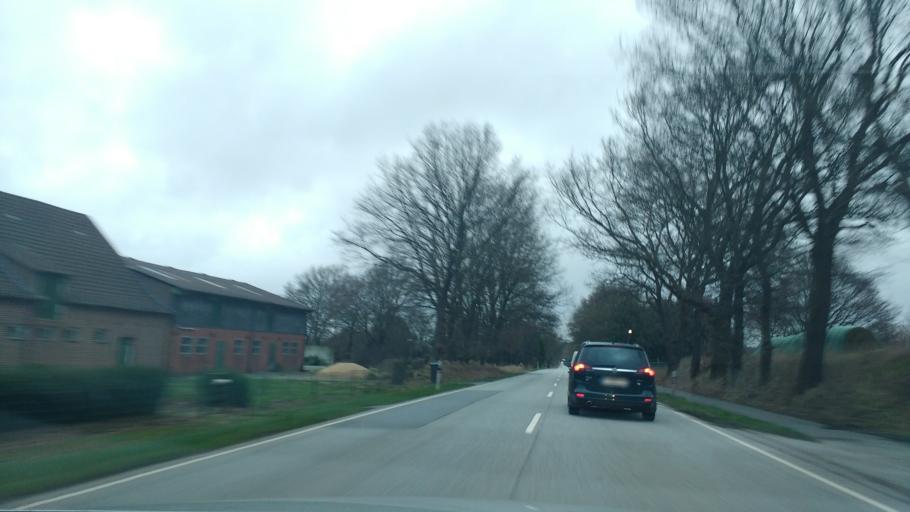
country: DE
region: Schleswig-Holstein
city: Schlotfeld
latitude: 53.9667
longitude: 9.5666
